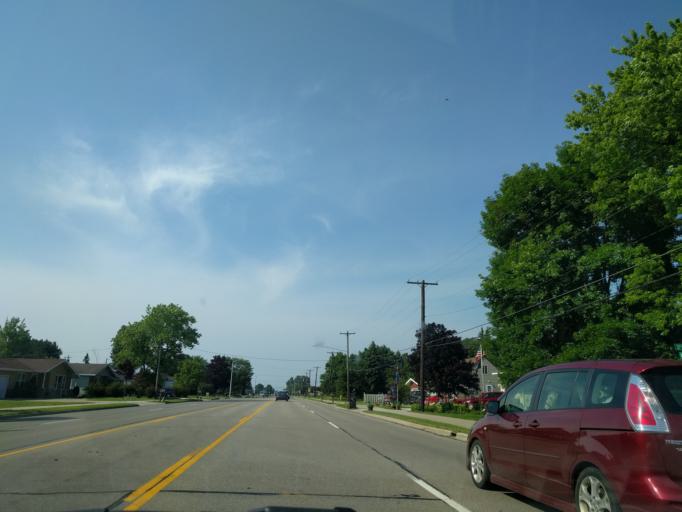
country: US
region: Michigan
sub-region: Delta County
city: Escanaba
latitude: 45.7319
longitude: -87.0800
